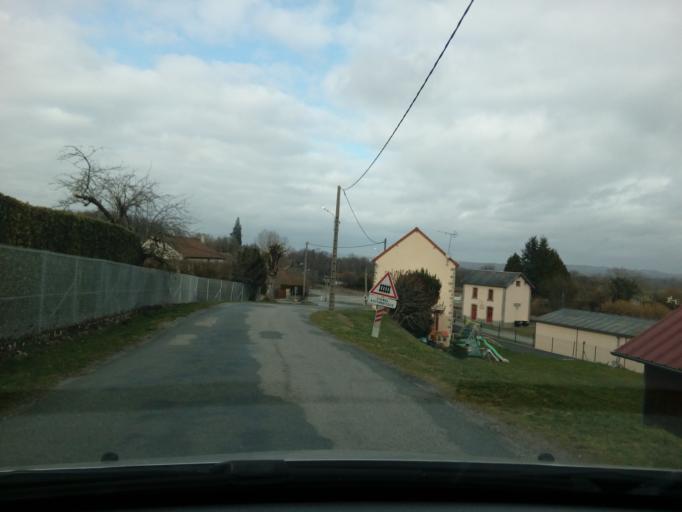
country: FR
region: Limousin
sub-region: Departement de la Creuse
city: Sainte-Feyre
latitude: 46.1400
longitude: 1.9246
